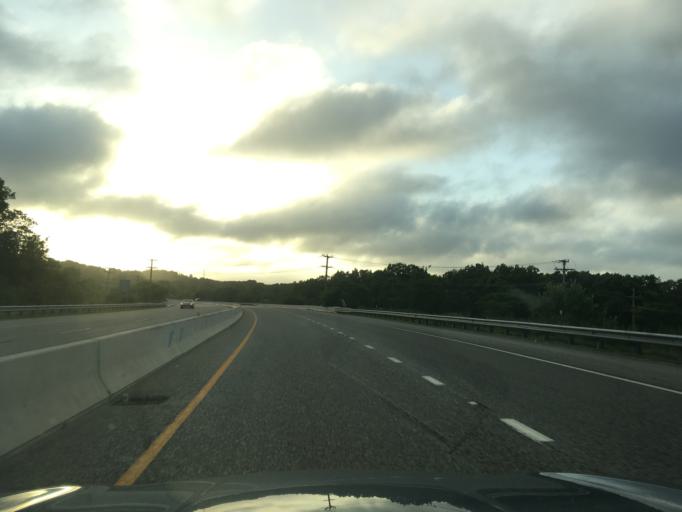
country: US
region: Rhode Island
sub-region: Kent County
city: East Greenwich
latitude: 41.6280
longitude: -71.4784
